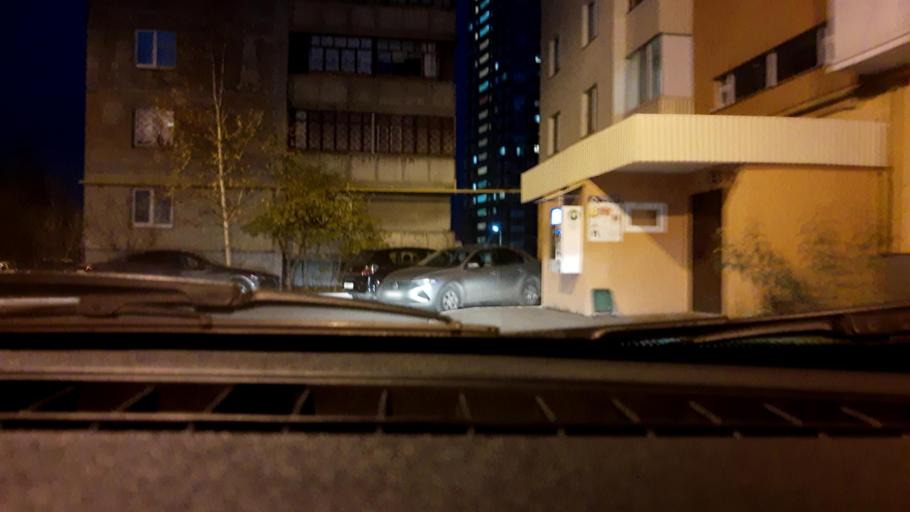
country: RU
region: Bashkortostan
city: Mikhaylovka
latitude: 54.7902
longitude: 55.8681
